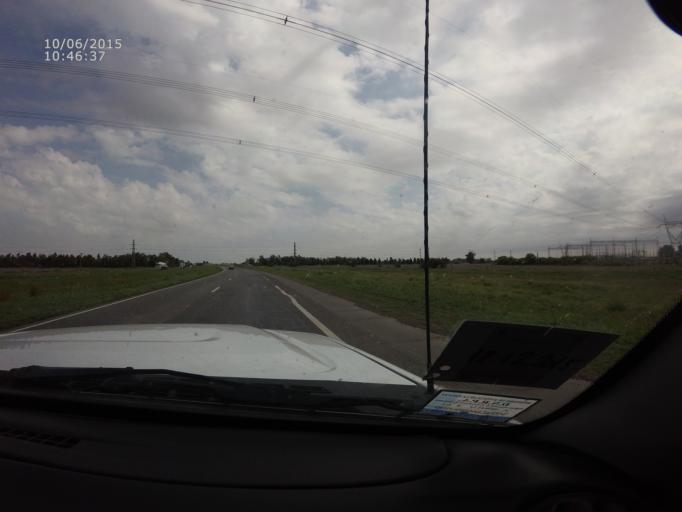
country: AR
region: Buenos Aires
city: San Nicolas de los Arroyos
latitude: -33.4147
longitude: -60.1832
